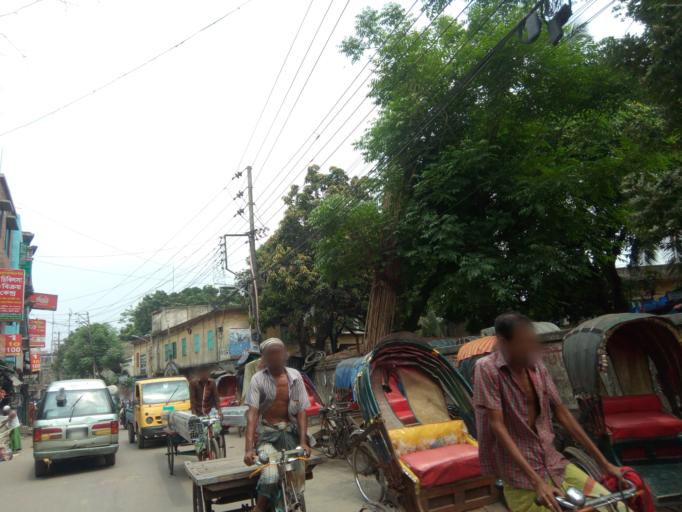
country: BD
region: Dhaka
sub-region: Dhaka
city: Dhaka
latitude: 23.6935
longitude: 90.4263
